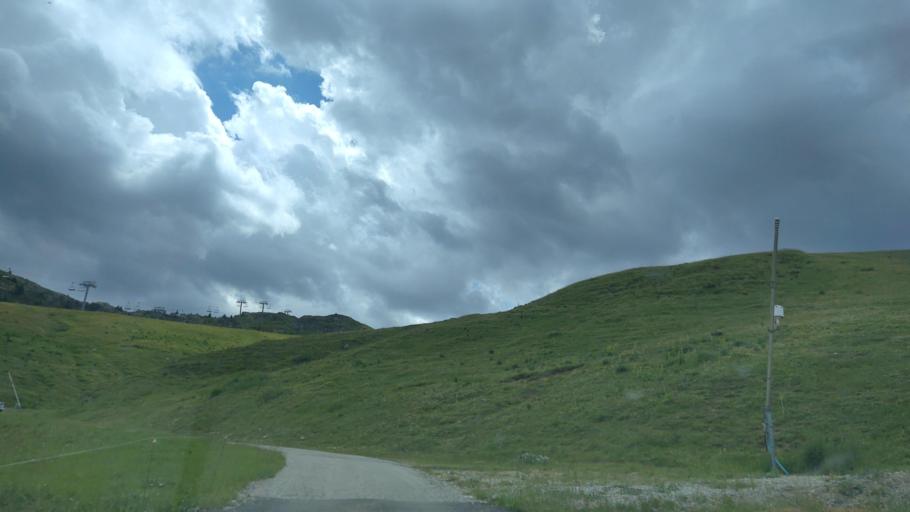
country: FR
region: Rhone-Alpes
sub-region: Departement de la Savoie
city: Courchevel
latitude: 45.3943
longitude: 6.6539
